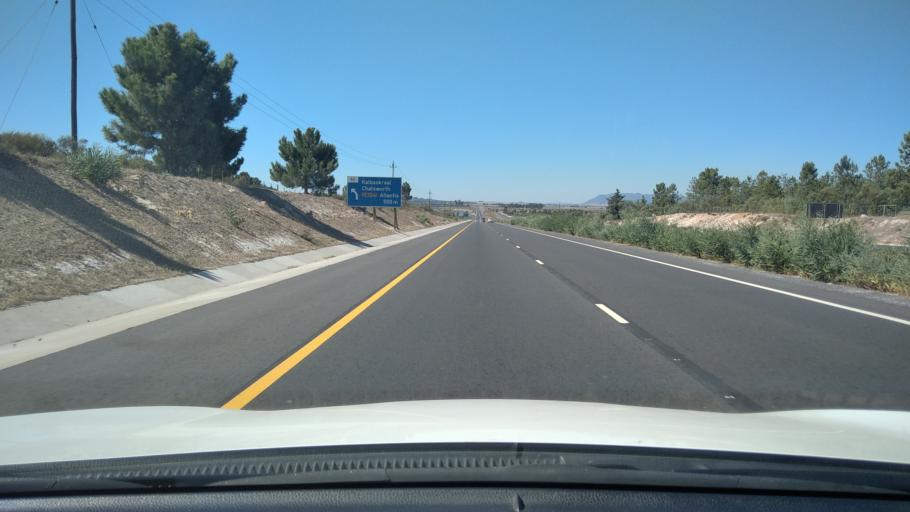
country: ZA
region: Western Cape
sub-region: City of Cape Town
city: Atlantis
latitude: -33.5880
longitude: 18.6086
